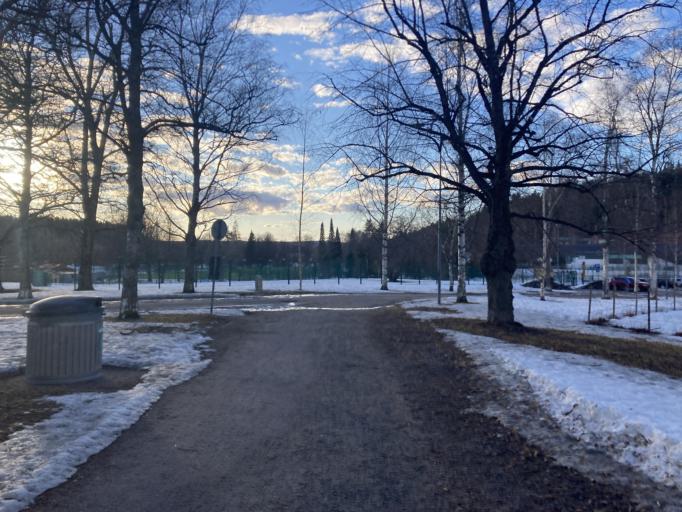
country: FI
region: Paijanne Tavastia
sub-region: Lahti
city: Lahti
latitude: 60.9873
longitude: 25.6542
